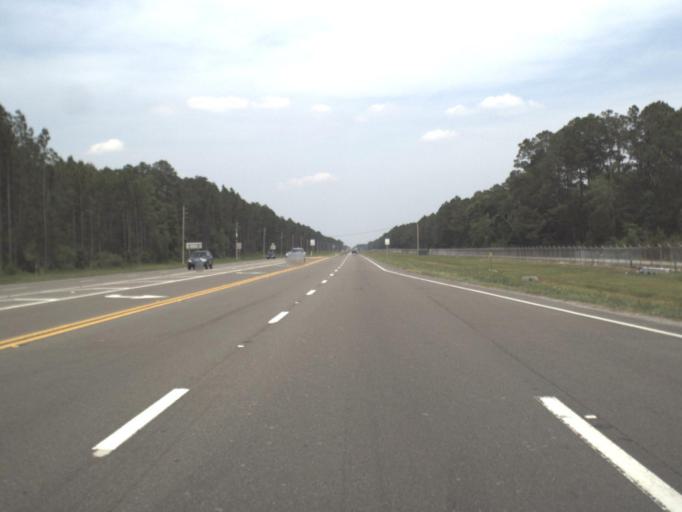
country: US
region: Florida
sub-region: Duval County
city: Baldwin
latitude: 30.2460
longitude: -81.8823
